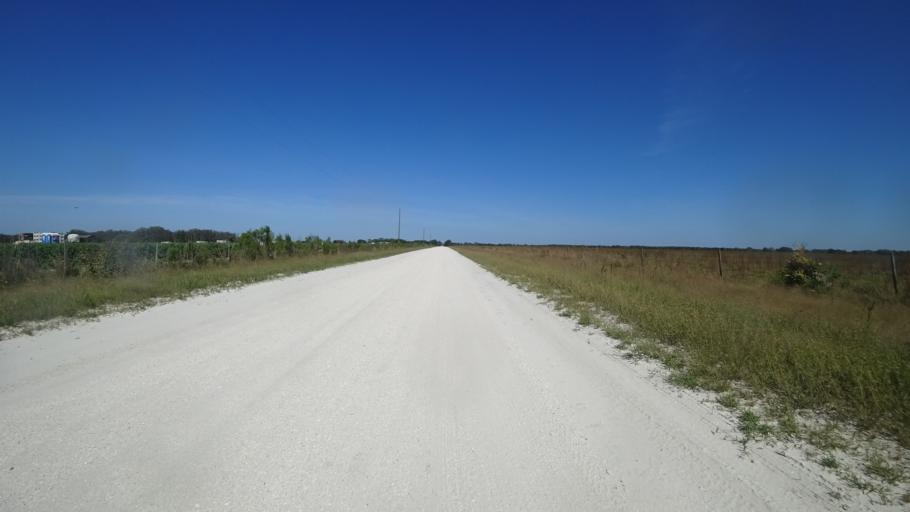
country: US
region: Florida
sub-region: DeSoto County
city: Arcadia
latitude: 27.3062
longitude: -82.0805
